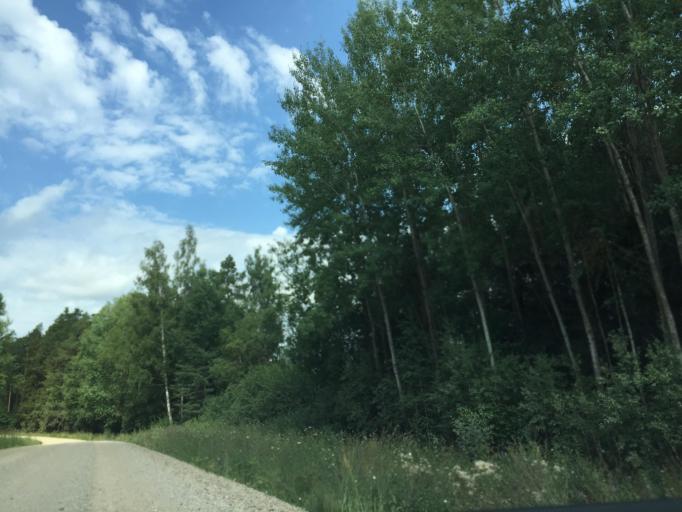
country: LV
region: Kandava
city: Kandava
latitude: 57.0074
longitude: 22.8437
